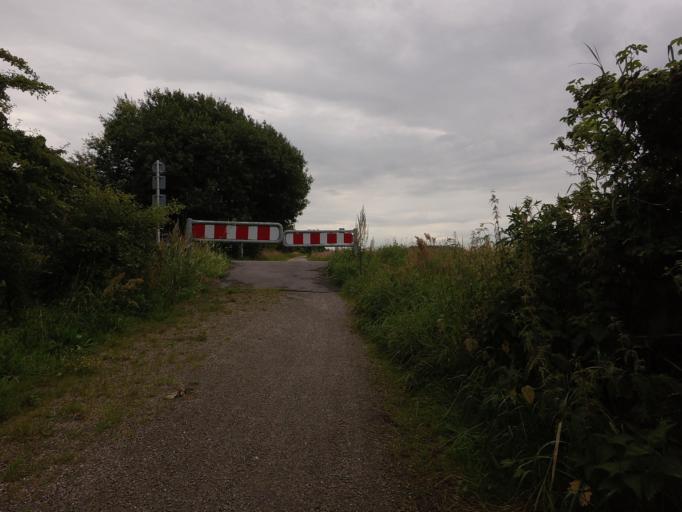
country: DK
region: North Denmark
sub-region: Alborg Kommune
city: Vadum
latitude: 57.1121
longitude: 9.8824
